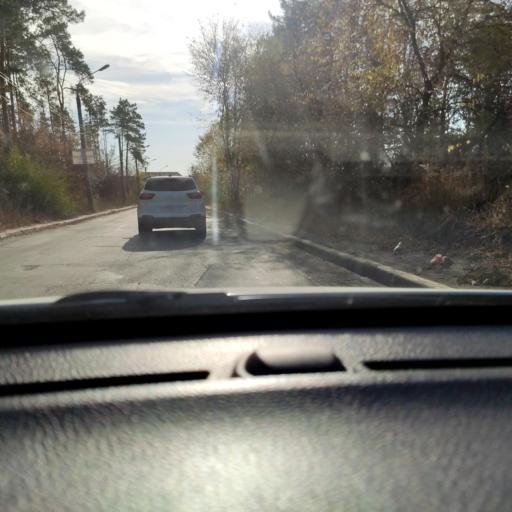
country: RU
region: Voronezj
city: Pridonskoy
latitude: 51.6427
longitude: 39.1101
